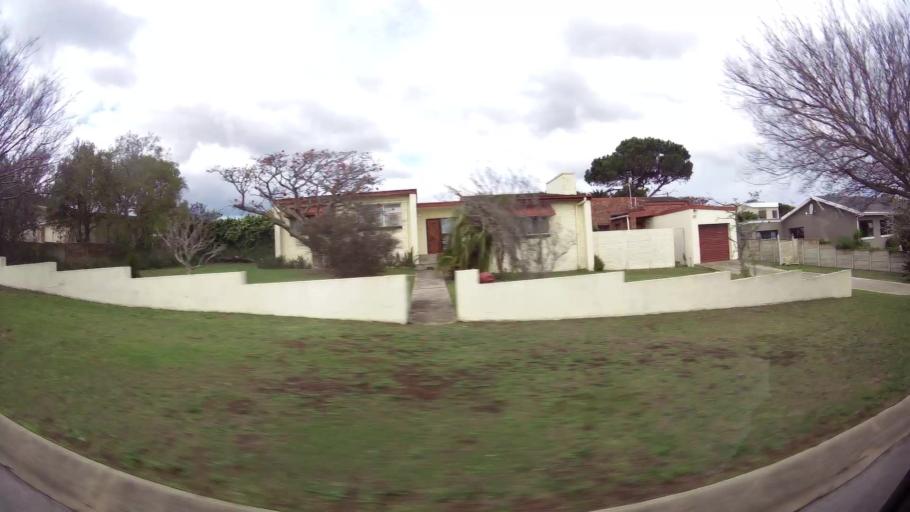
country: ZA
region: Eastern Cape
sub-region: Nelson Mandela Bay Metropolitan Municipality
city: Port Elizabeth
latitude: -33.9345
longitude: 25.5239
